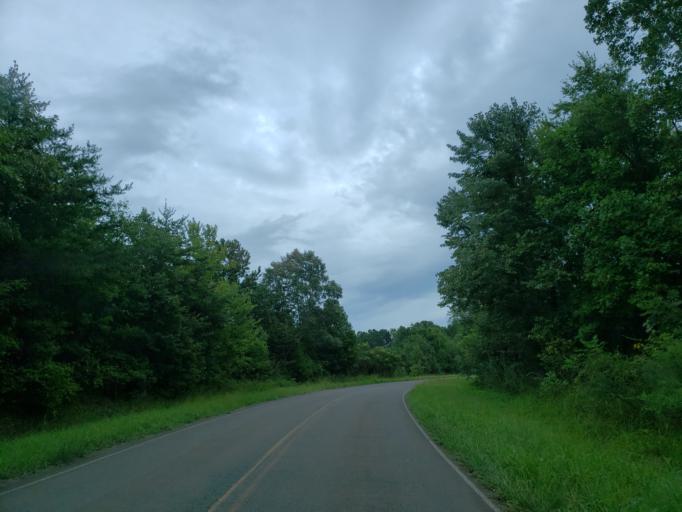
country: US
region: Georgia
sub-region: Pickens County
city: Jasper
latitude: 34.4234
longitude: -84.5762
